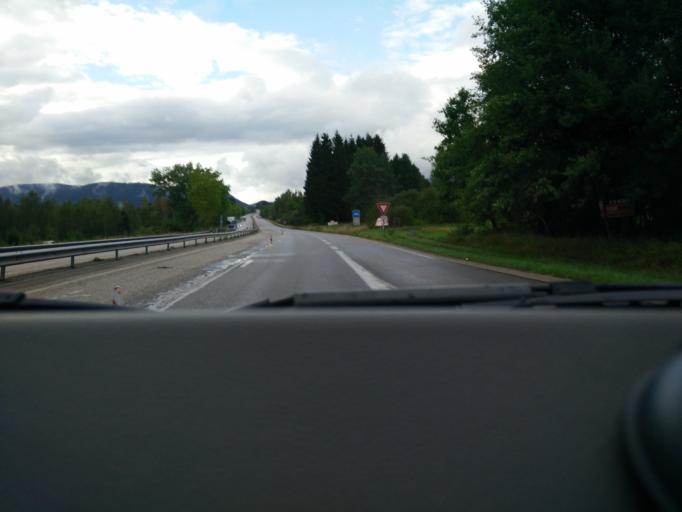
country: FR
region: Lorraine
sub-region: Departement des Vosges
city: Saint-Michel-sur-Meurthe
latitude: 48.3436
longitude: 6.8899
